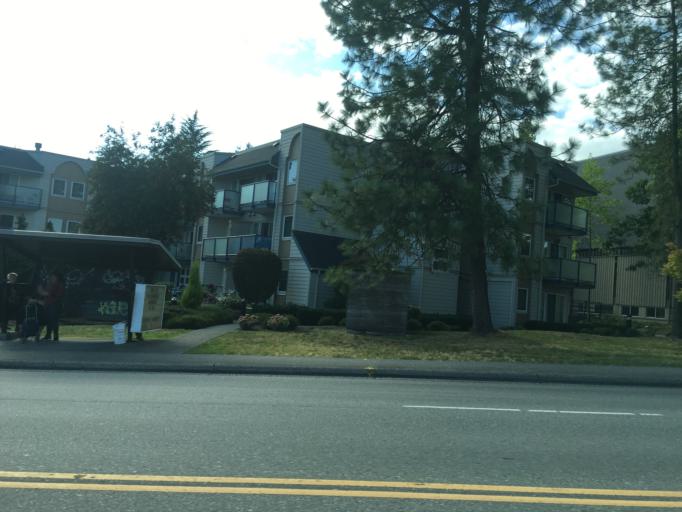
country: CA
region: British Columbia
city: Port Moody
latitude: 49.2477
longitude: -122.8707
